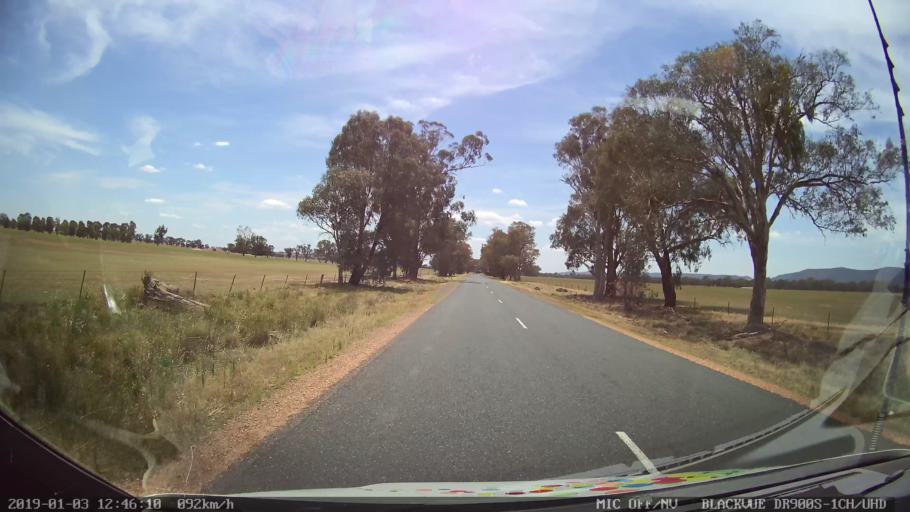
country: AU
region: New South Wales
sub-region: Weddin
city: Grenfell
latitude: -33.7410
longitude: 148.2302
